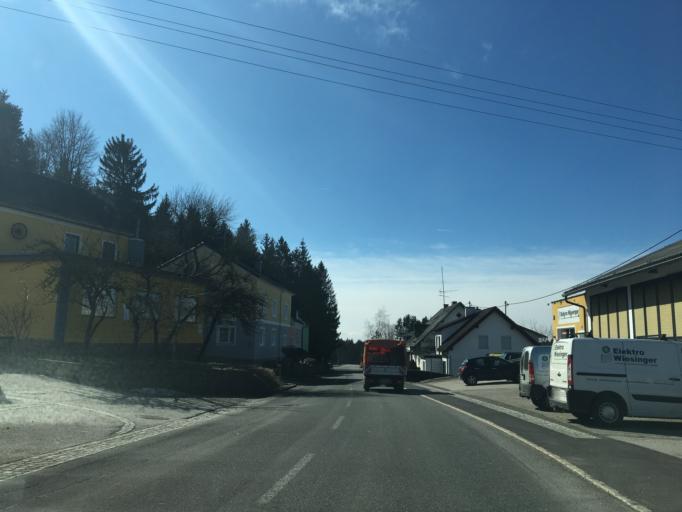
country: AT
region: Upper Austria
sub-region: Politischer Bezirk Perg
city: Sankt Georgen am Walde
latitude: 48.3049
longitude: 14.9065
